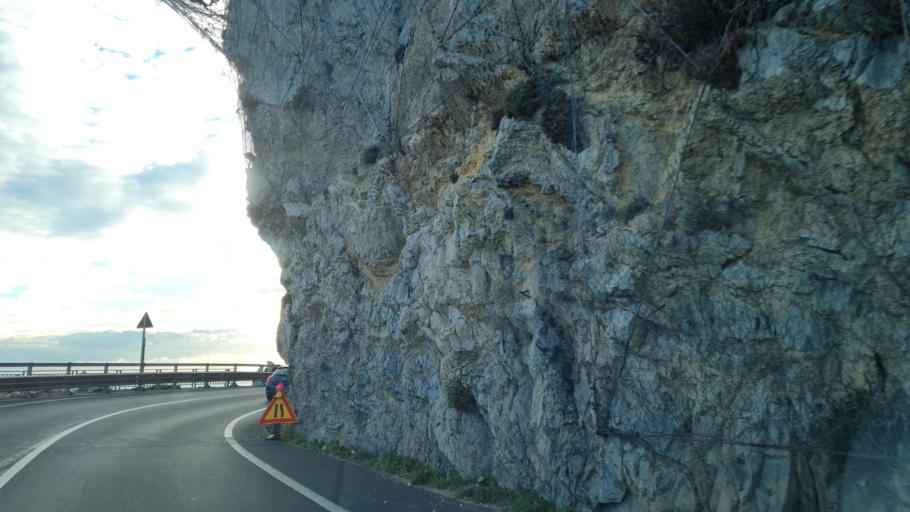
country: IT
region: Liguria
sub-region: Provincia di Savona
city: Noli
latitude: 44.1951
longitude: 8.4247
